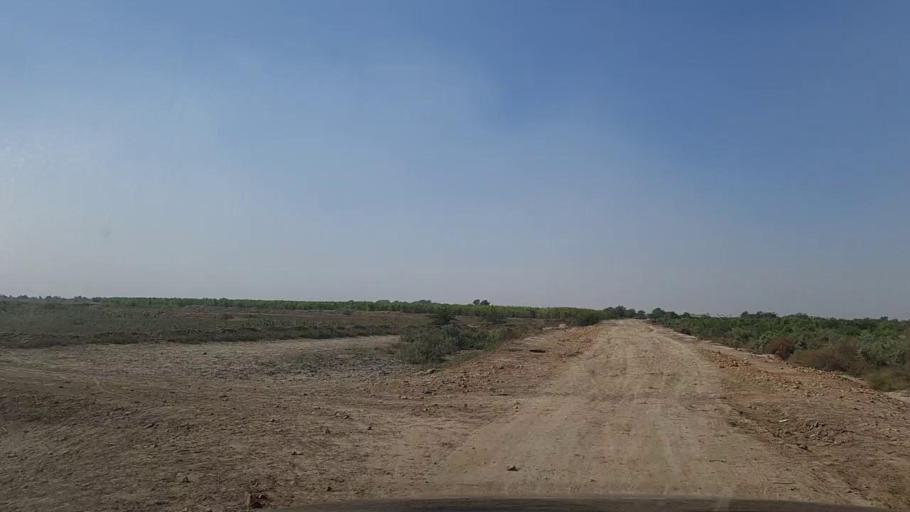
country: PK
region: Sindh
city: Daro Mehar
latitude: 24.8373
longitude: 68.1376
